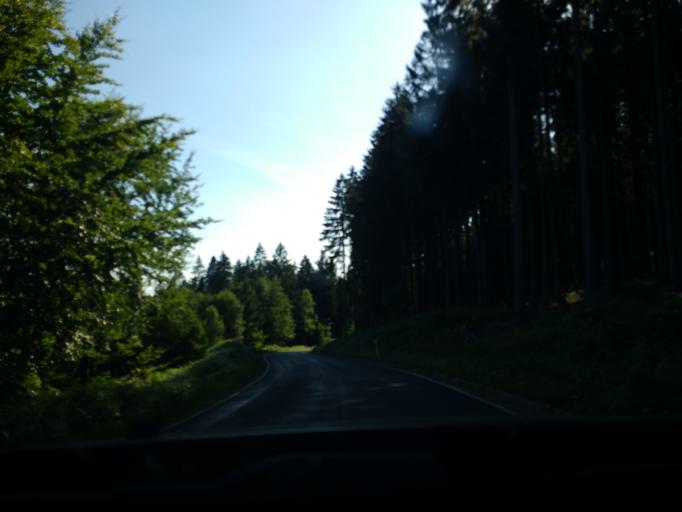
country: DE
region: Rheinland-Pfalz
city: Densborn
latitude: 50.1292
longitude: 6.6341
